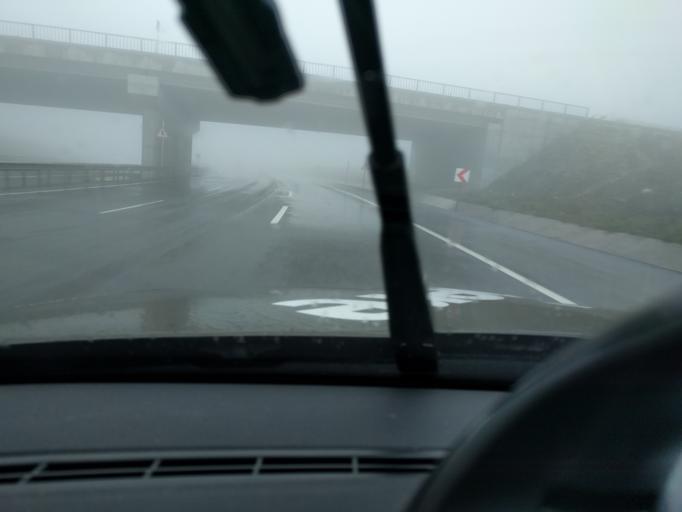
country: TR
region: Istanbul
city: Boyalik
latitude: 41.2488
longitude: 28.5883
